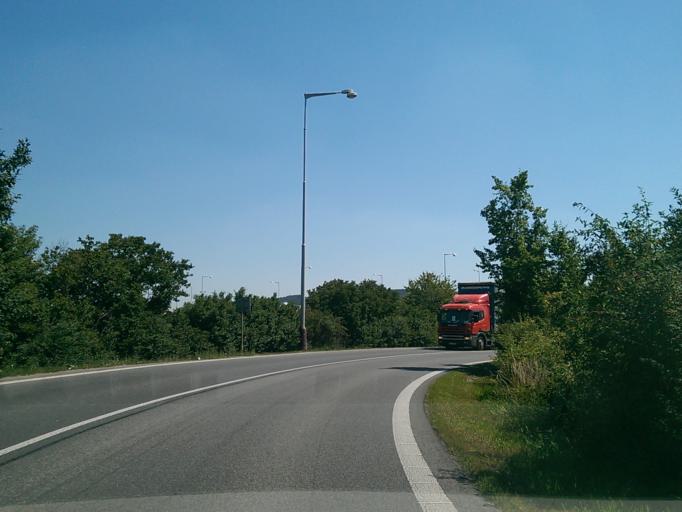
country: CZ
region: Central Bohemia
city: Kosmonosy
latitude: 50.4106
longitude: 14.9421
